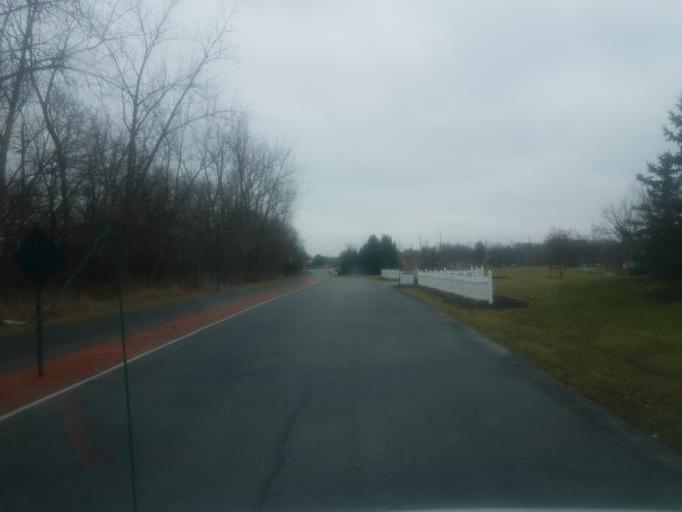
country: US
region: Ohio
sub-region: Franklin County
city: Westerville
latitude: 40.1275
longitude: -82.9470
